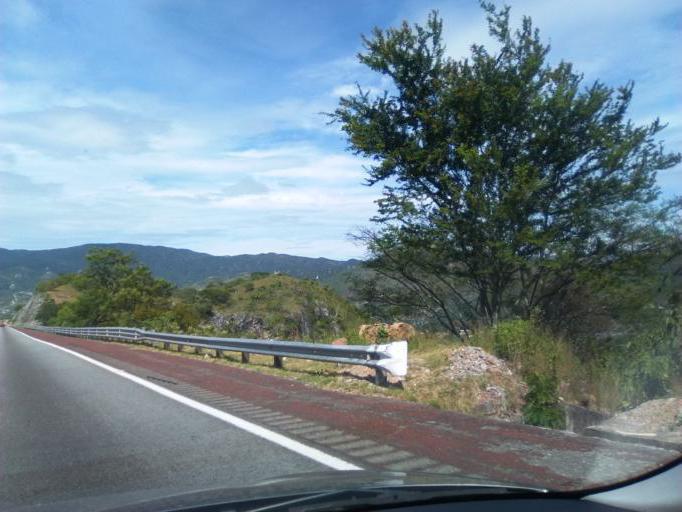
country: MX
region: Guerrero
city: Petaquillas
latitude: 17.4663
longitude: -99.4734
